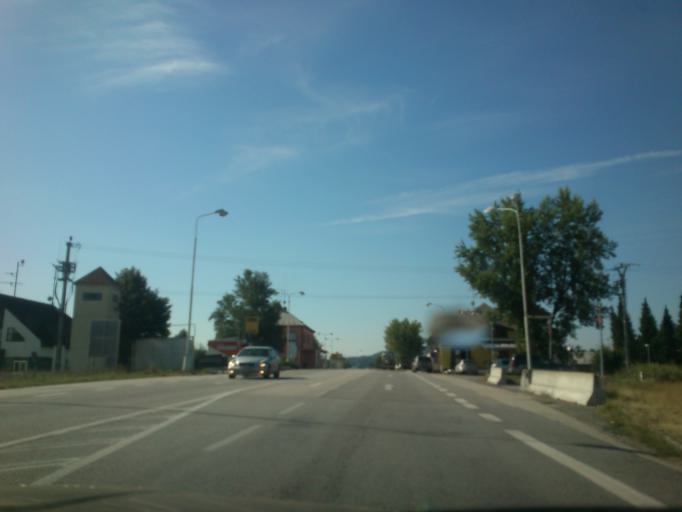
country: CZ
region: Jihocesky
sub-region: Okres Cesky Krumlov
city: Dolni Dvoriste
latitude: 48.6517
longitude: 14.4527
